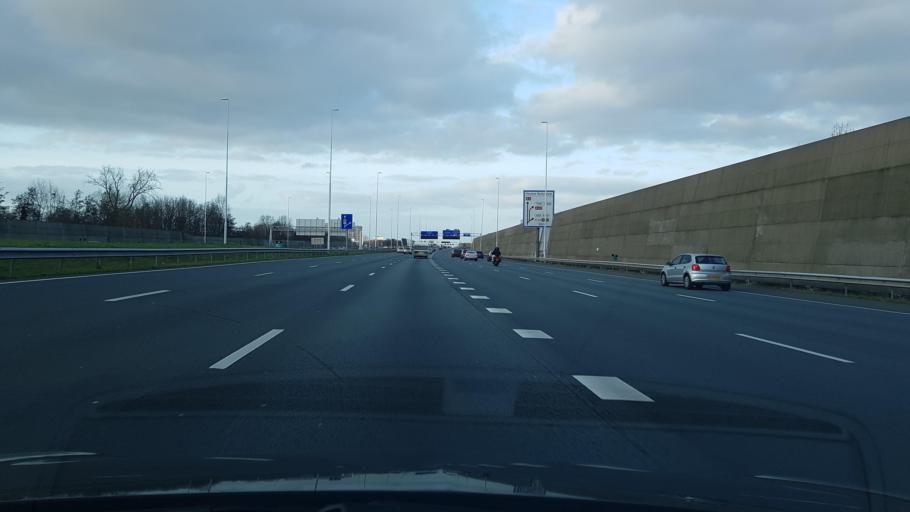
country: NL
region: South Holland
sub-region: Gemeente Vlaardingen
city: Vlaardingen
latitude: 51.8991
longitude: 4.3596
